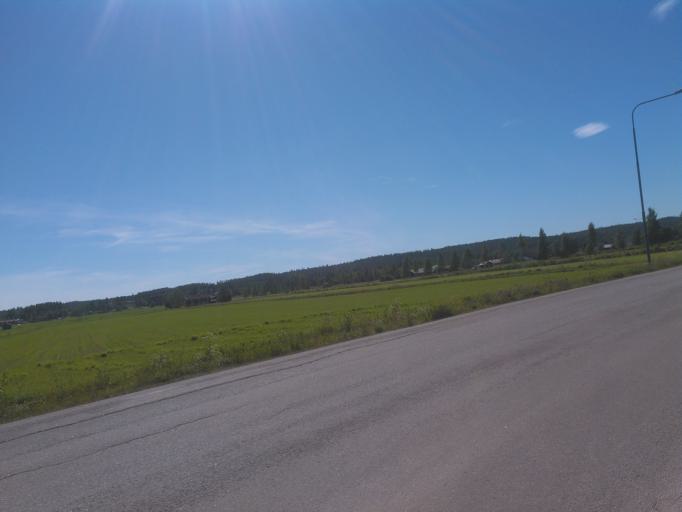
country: SE
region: Vaesterbotten
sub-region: Umea Kommun
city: Roback
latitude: 63.8198
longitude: 20.1986
